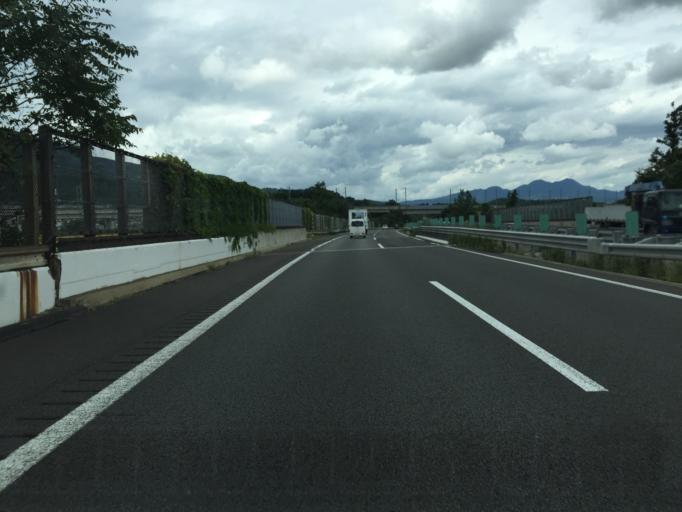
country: JP
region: Miyagi
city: Shiroishi
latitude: 37.9687
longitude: 140.6153
